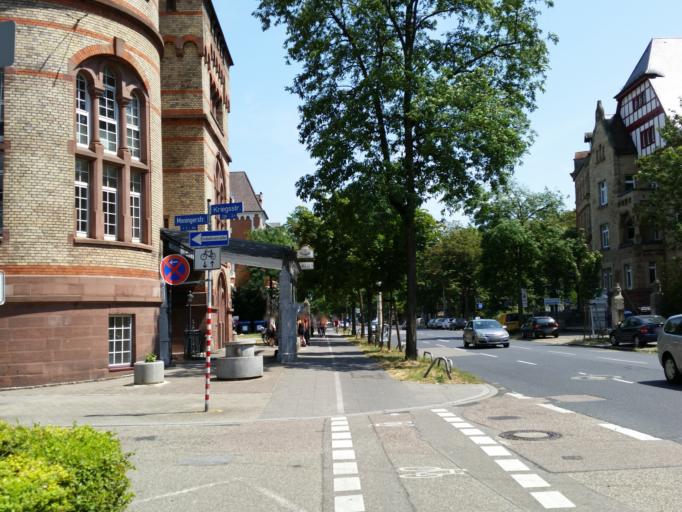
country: DE
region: Baden-Wuerttemberg
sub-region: Karlsruhe Region
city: Karlsruhe
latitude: 49.0054
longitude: 8.3829
